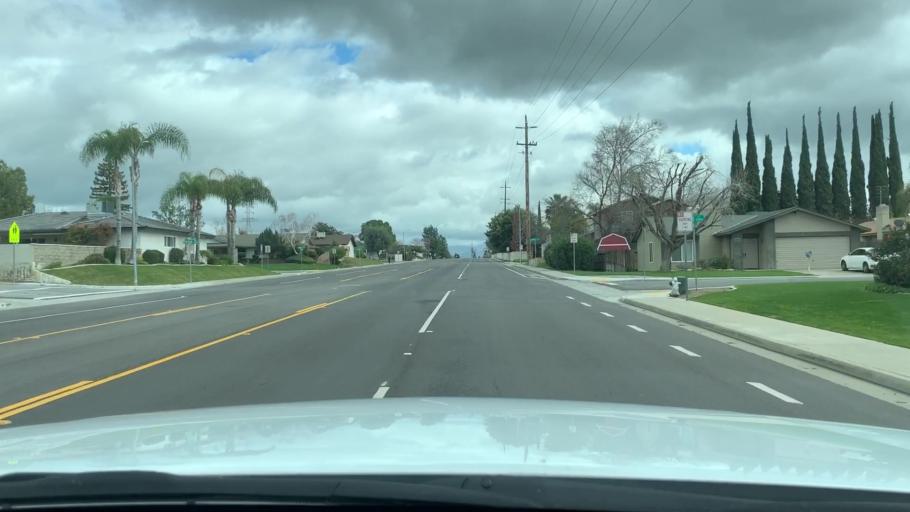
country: US
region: California
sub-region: Kern County
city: Bakersfield
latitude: 35.3978
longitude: -118.9368
